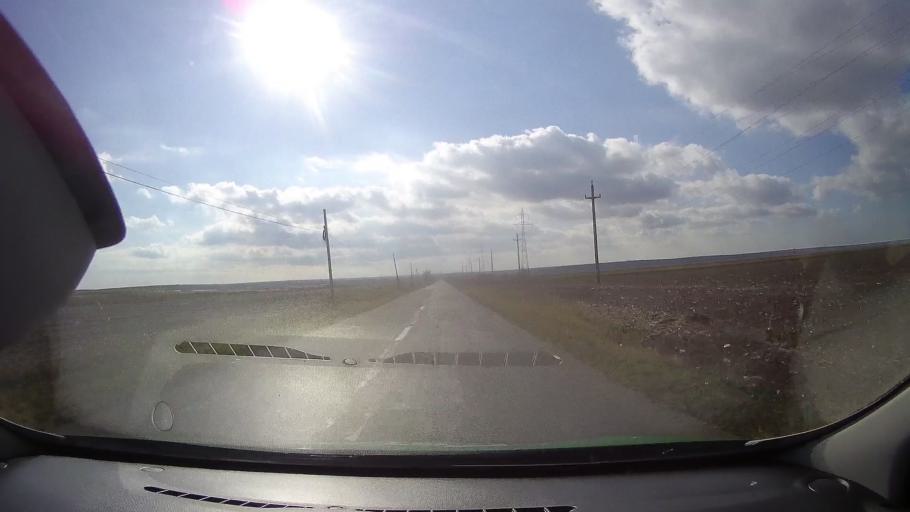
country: RO
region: Constanta
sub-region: Comuna Istria
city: Istria
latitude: 44.5410
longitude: 28.6897
